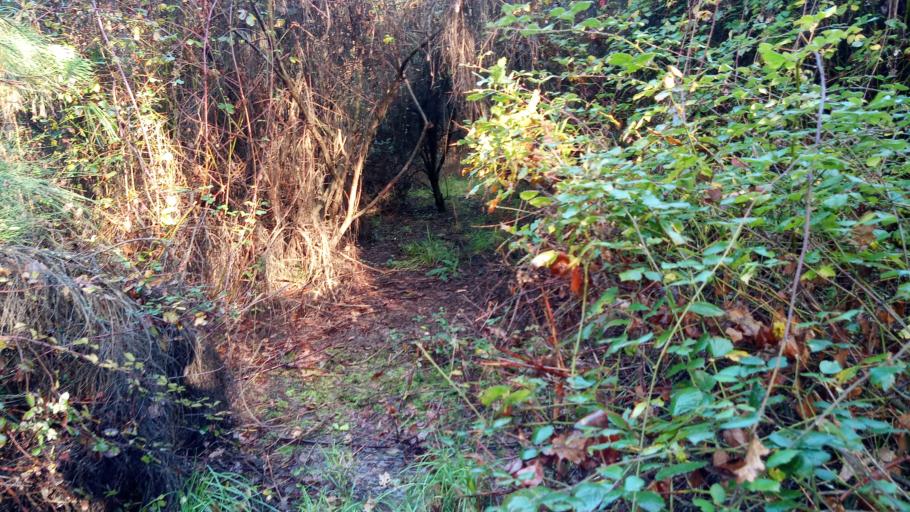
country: PT
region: Viana do Castelo
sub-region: Paredes de Coura
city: Paredes de Coura
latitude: 41.8982
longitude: -8.6152
